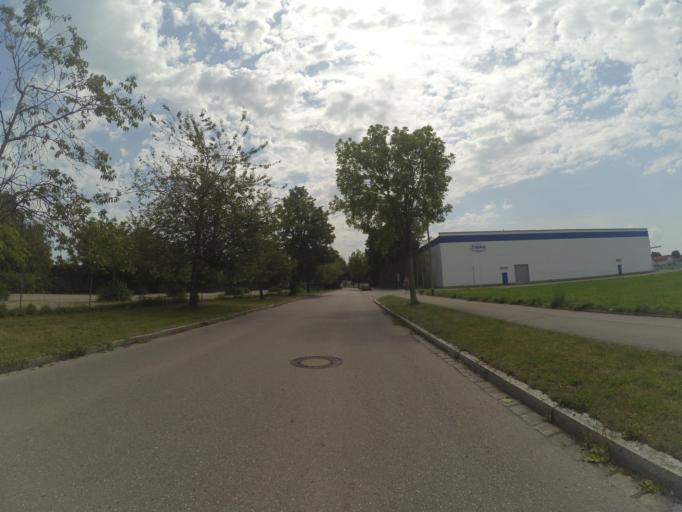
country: DE
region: Bavaria
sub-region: Swabia
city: Buchloe
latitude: 48.0423
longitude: 10.7169
